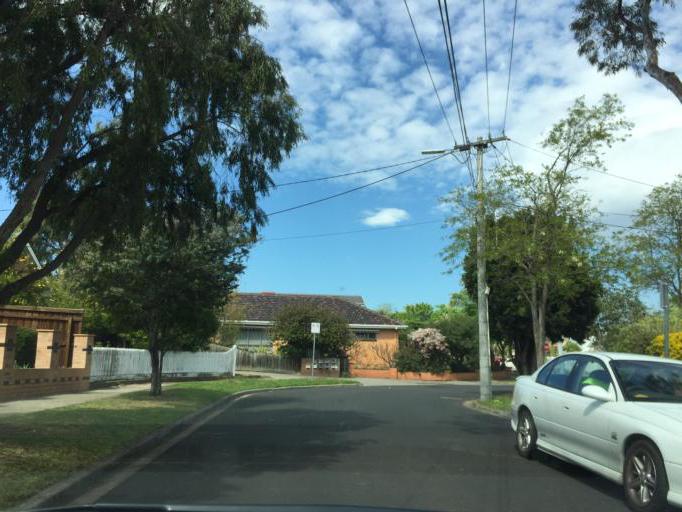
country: AU
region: Victoria
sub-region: Maribyrnong
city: Maribyrnong
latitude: -37.7903
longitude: 144.8845
